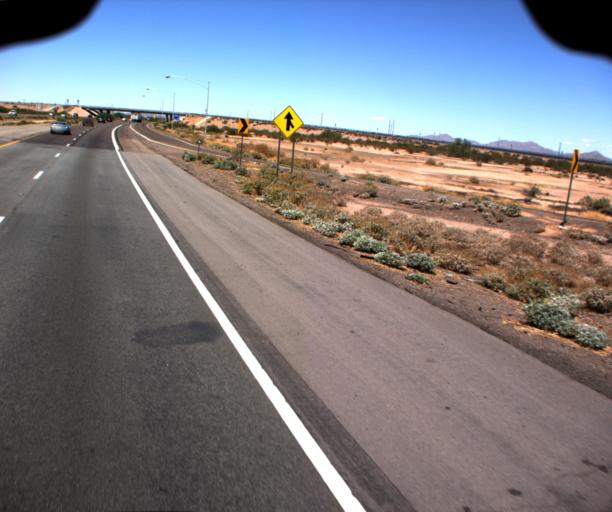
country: US
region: Arizona
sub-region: Pinal County
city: Arizona City
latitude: 32.8161
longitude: -111.6808
